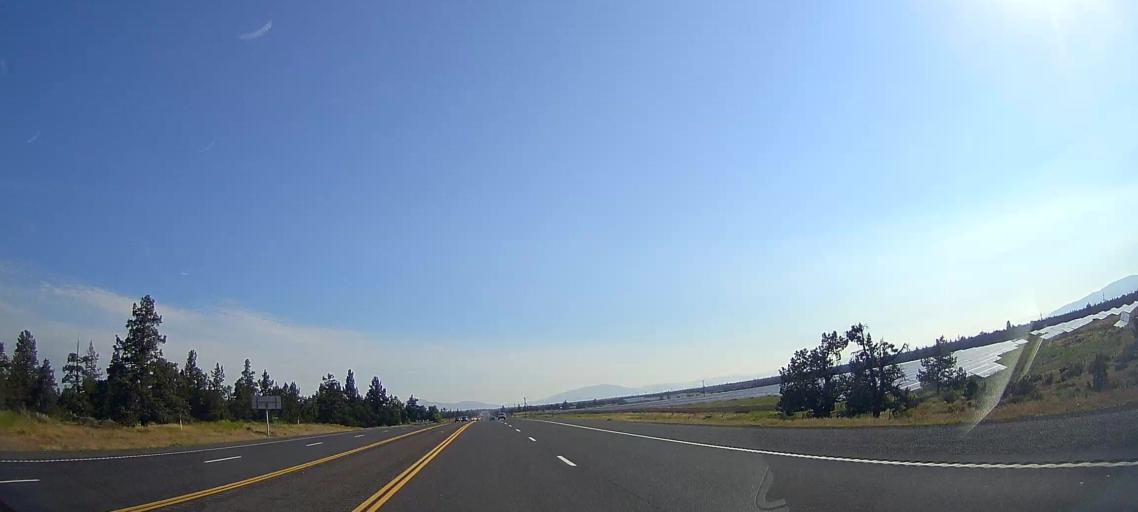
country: US
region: Oregon
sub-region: Deschutes County
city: Redmond
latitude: 44.1870
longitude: -121.2397
